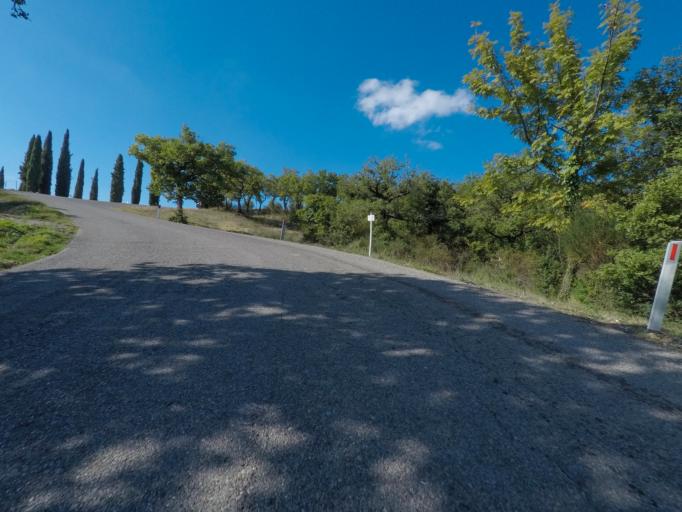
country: IT
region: Tuscany
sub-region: Provincia di Siena
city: Radda in Chianti
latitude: 43.5160
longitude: 11.4062
